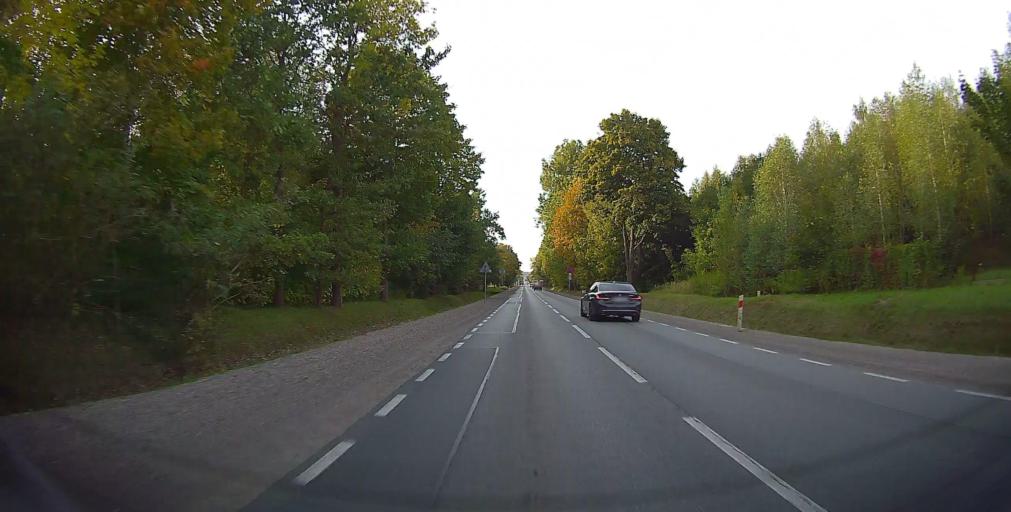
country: PL
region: Masovian Voivodeship
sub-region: Powiat piaseczynski
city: Zabieniec
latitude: 52.0562
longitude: 21.0531
